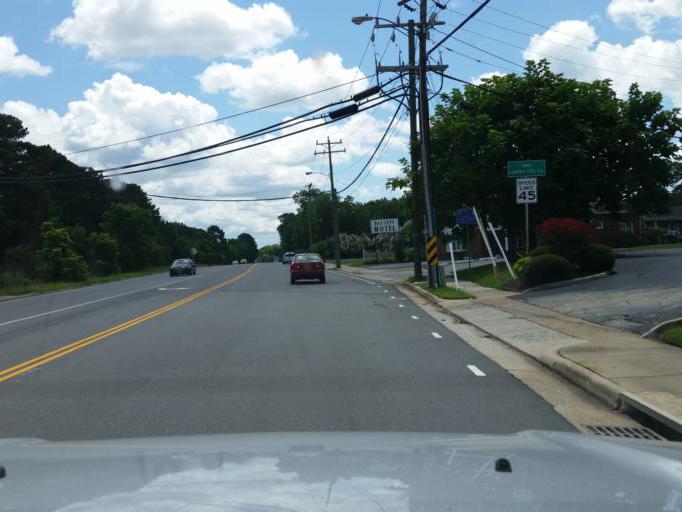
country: US
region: Virginia
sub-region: City of Williamsburg
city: Williamsburg
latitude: 37.2659
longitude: -76.6807
